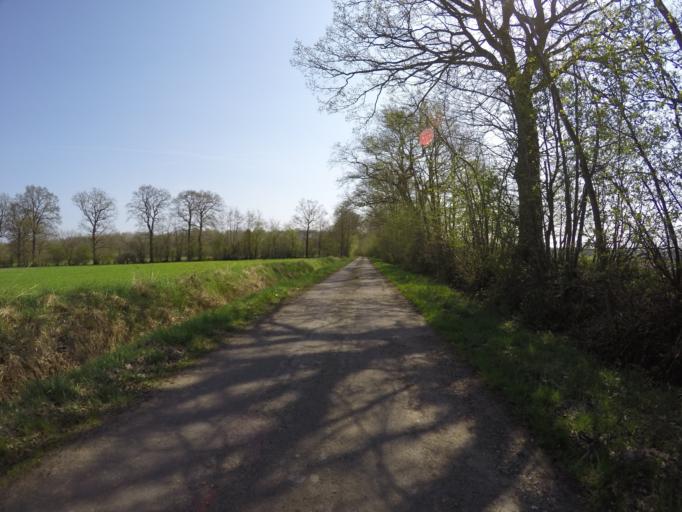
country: DE
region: Schleswig-Holstein
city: Hemdingen
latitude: 53.7398
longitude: 9.8229
